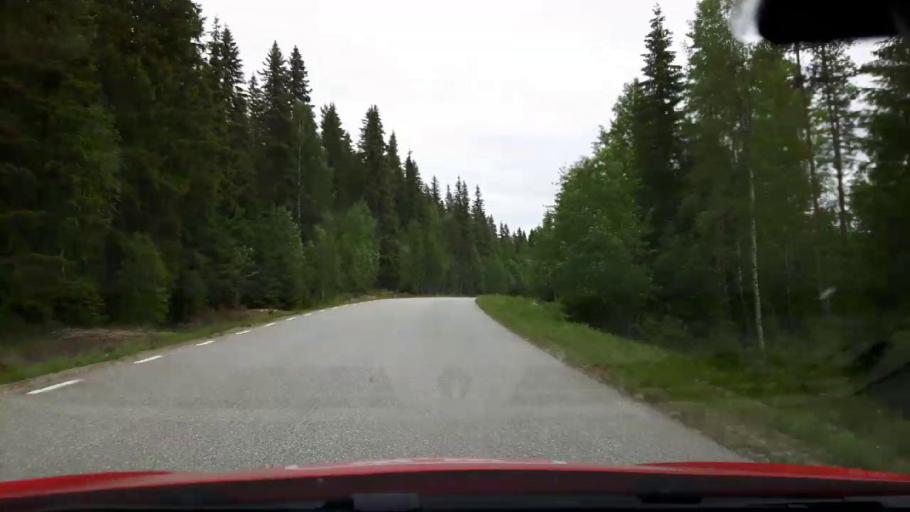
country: SE
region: Jaemtland
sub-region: Ragunda Kommun
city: Hammarstrand
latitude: 63.2142
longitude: 15.9756
